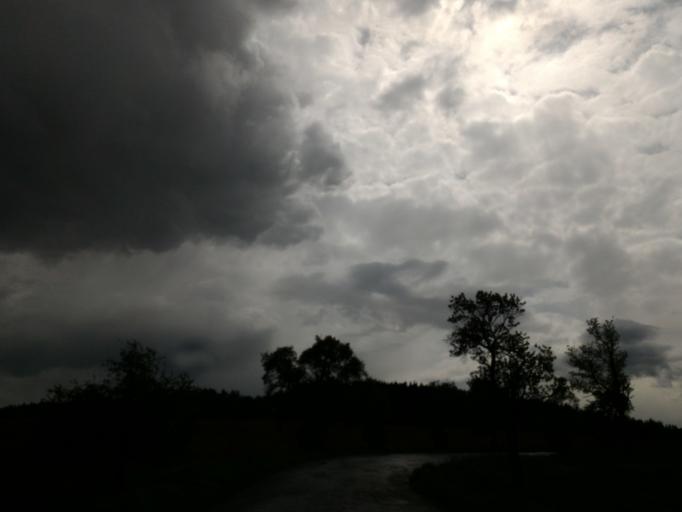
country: CZ
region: Vysocina
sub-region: Okres Havlickuv Brod
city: Svetla nad Sazavou
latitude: 49.6329
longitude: 15.3675
